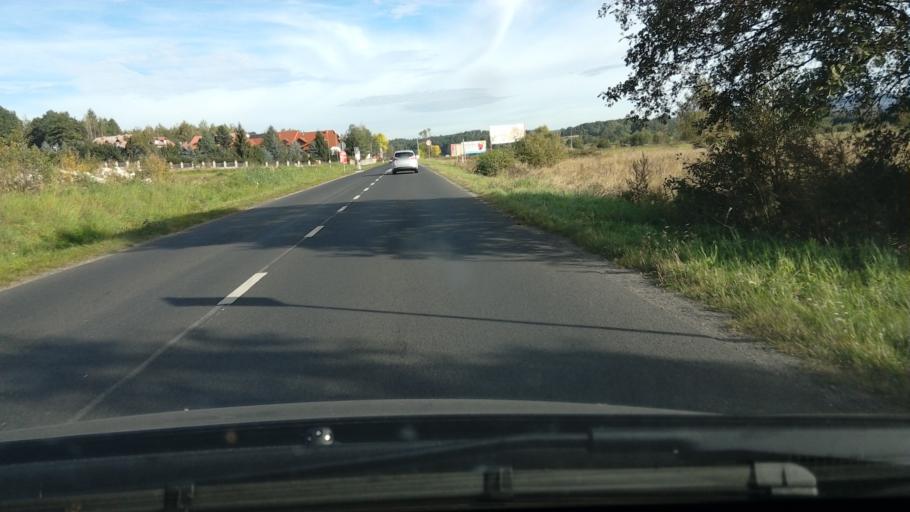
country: PL
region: Lower Silesian Voivodeship
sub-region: Powiat jeleniogorski
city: Myslakowice
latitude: 50.8490
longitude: 15.7735
